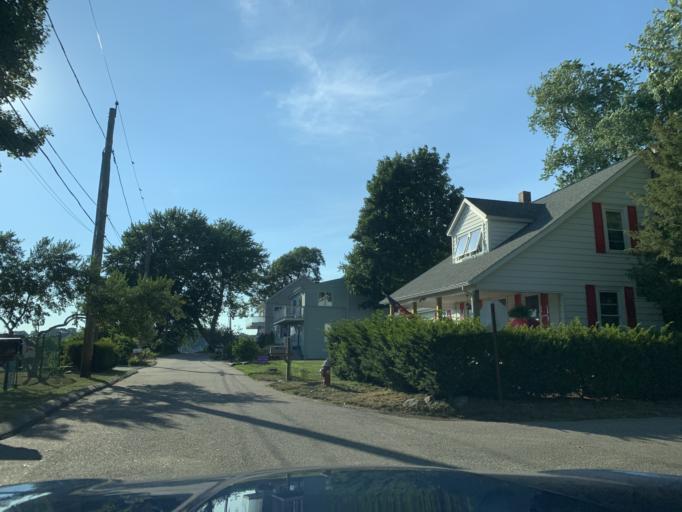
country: US
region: Rhode Island
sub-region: Kent County
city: Warwick
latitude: 41.6880
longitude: -71.4417
